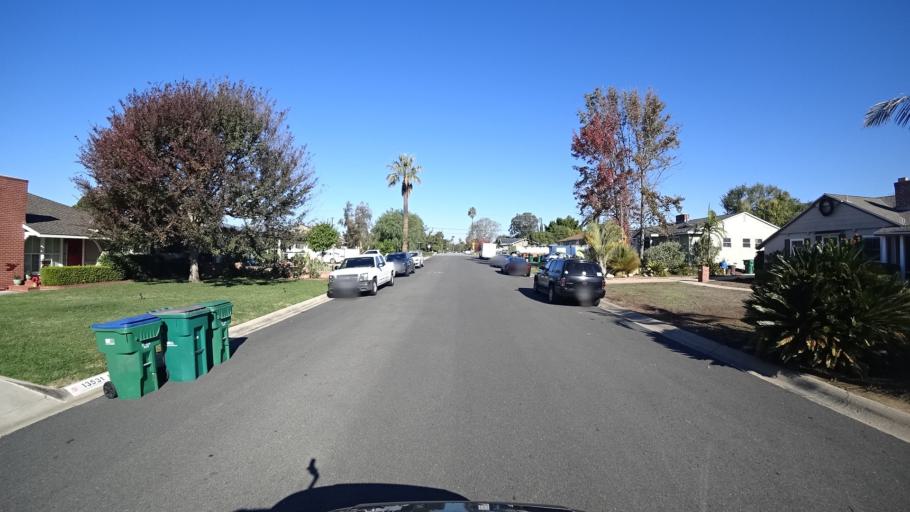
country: US
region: California
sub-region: Orange County
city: North Tustin
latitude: 33.7657
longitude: -117.8095
